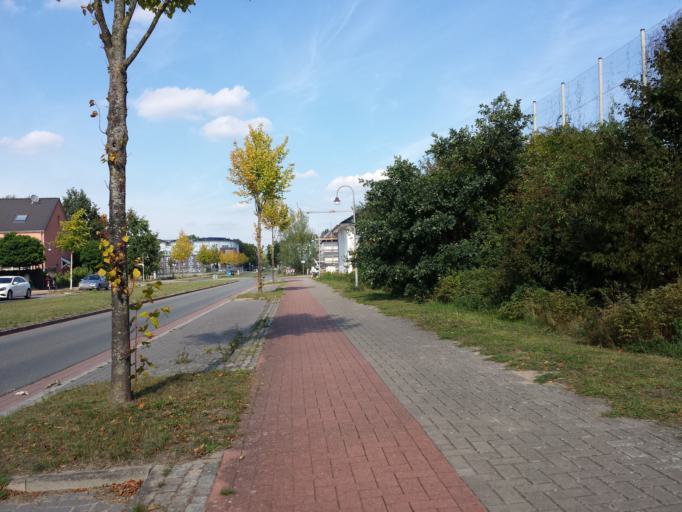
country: DE
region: Bremen
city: Bremen
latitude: 53.0305
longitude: 8.8319
